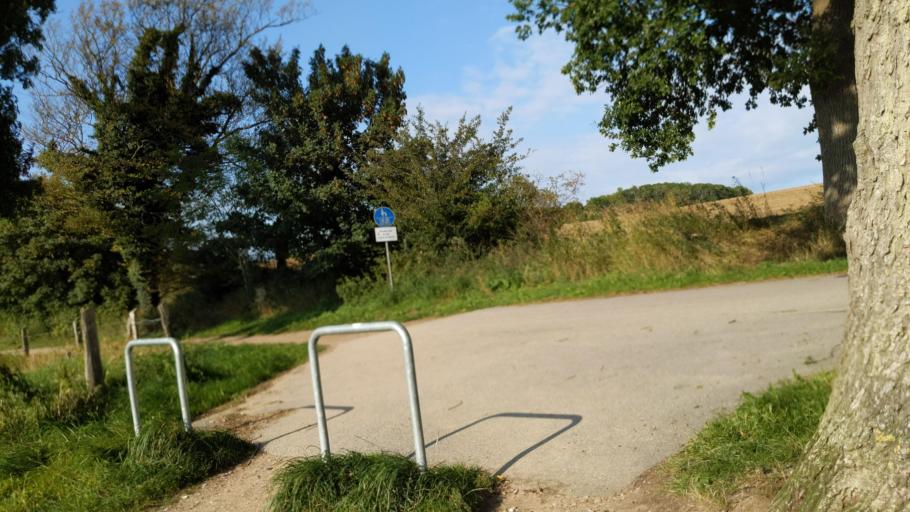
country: DE
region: Mecklenburg-Vorpommern
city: Kalkhorst
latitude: 54.0034
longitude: 11.0433
